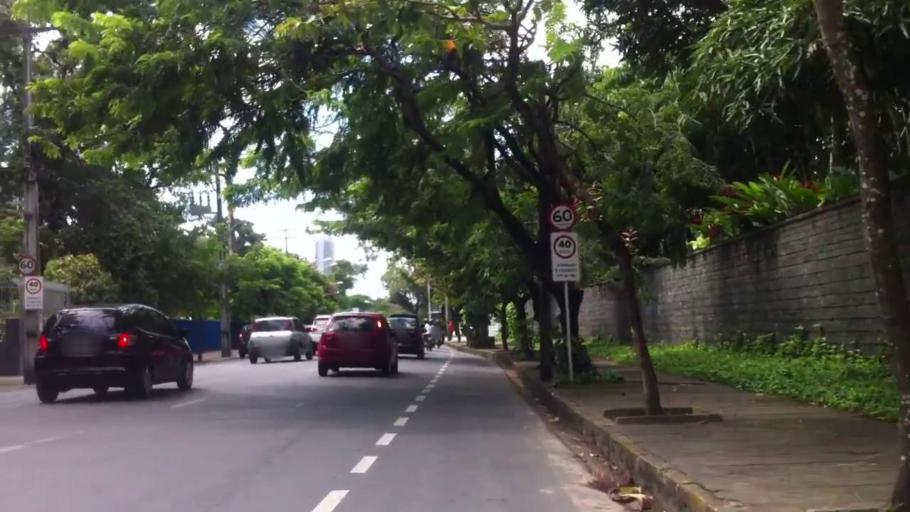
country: BR
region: Pernambuco
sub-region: Recife
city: Recife
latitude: -8.0370
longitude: -34.9062
